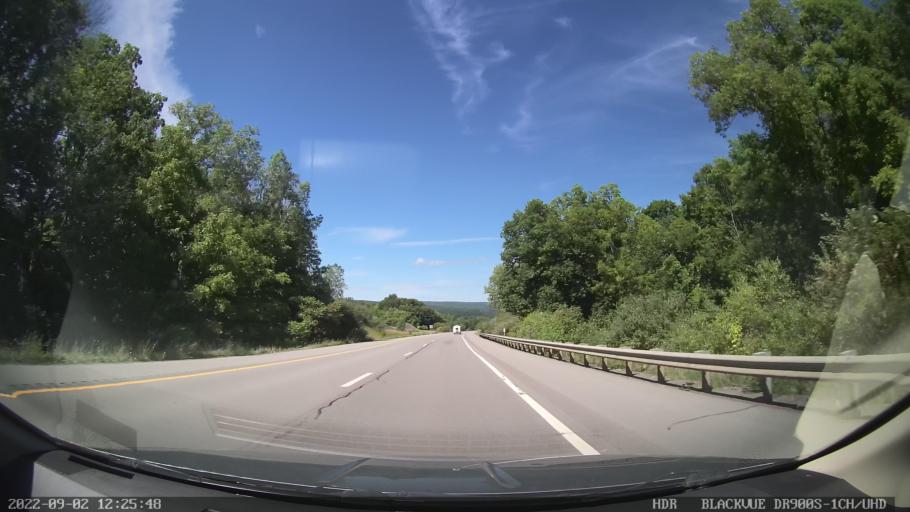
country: US
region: New York
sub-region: Livingston County
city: Dansville
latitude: 42.5335
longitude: -77.6755
